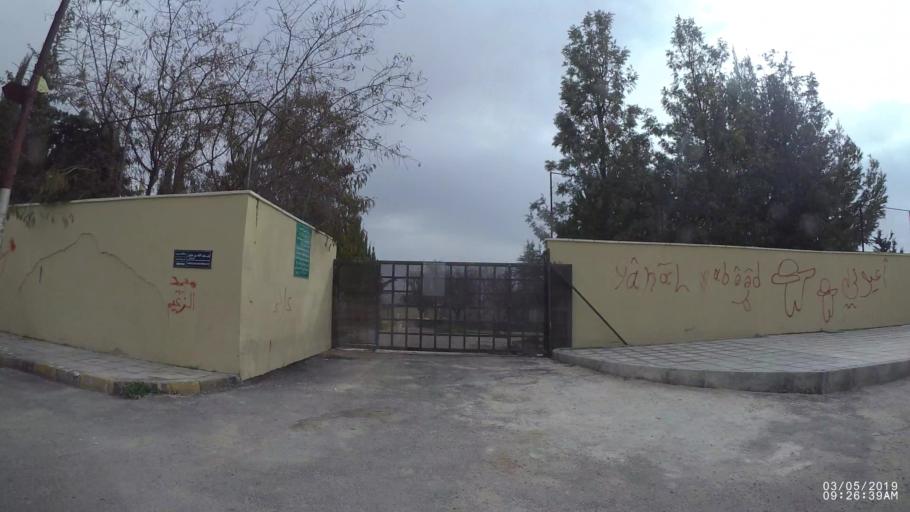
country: JO
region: Amman
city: Amman
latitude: 31.9707
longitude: 35.9345
